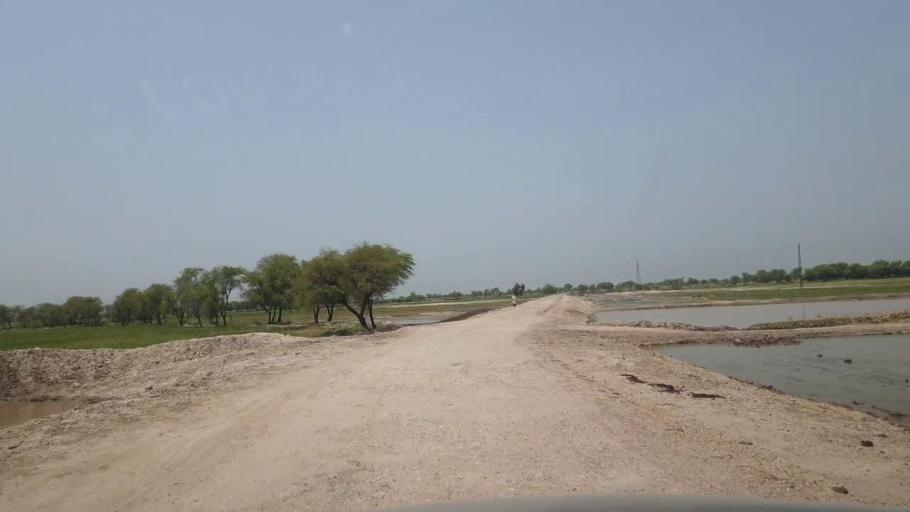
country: PK
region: Sindh
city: Garhi Yasin
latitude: 27.8702
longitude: 68.4525
